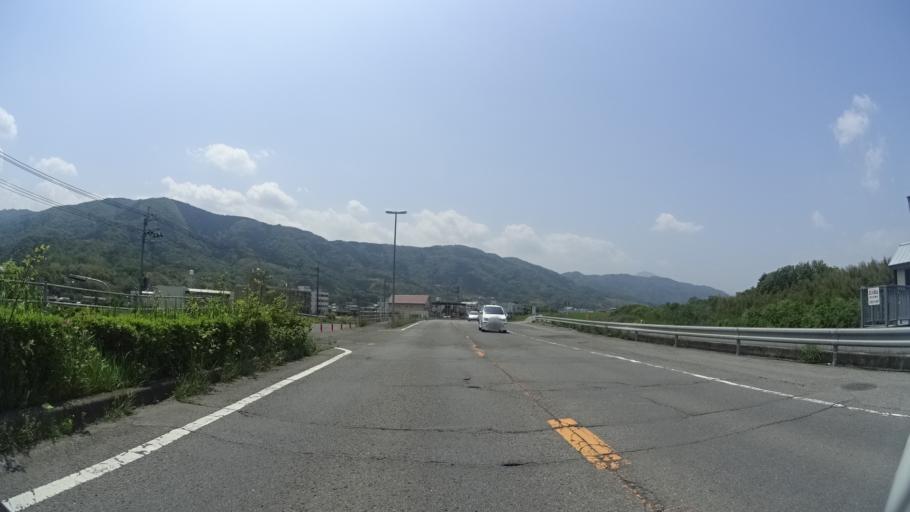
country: JP
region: Tokushima
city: Kamojimacho-jogejima
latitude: 34.0631
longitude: 134.3170
